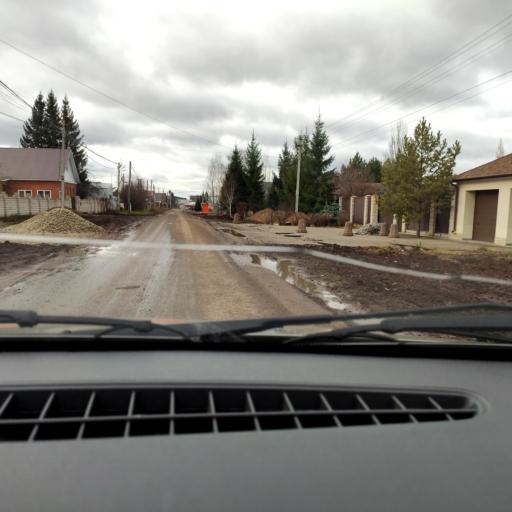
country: RU
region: Bashkortostan
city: Avdon
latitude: 54.4965
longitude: 55.8718
